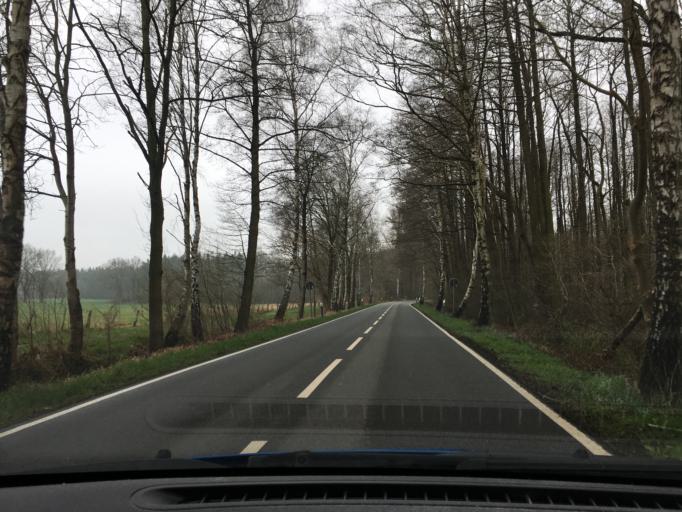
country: DE
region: Lower Saxony
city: Thomasburg
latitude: 53.2306
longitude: 10.6538
